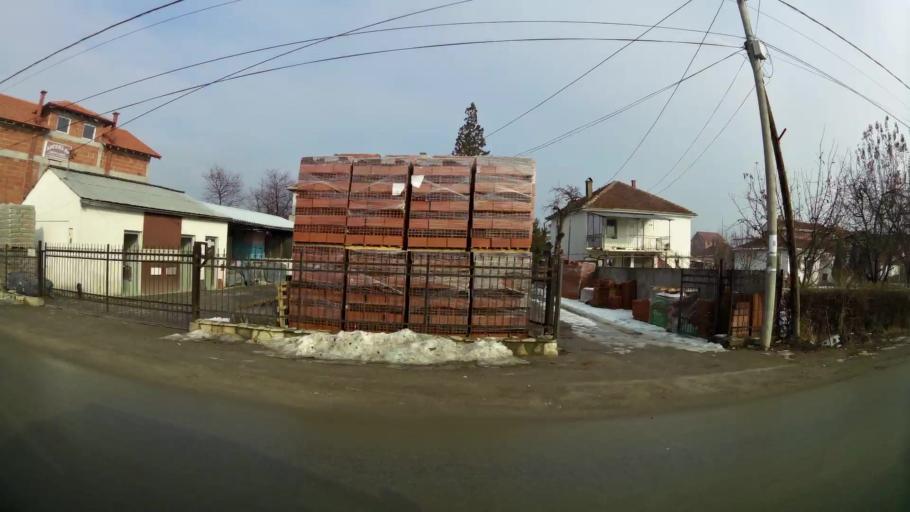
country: MK
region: Ilinden
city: Marino
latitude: 41.9941
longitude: 21.5884
